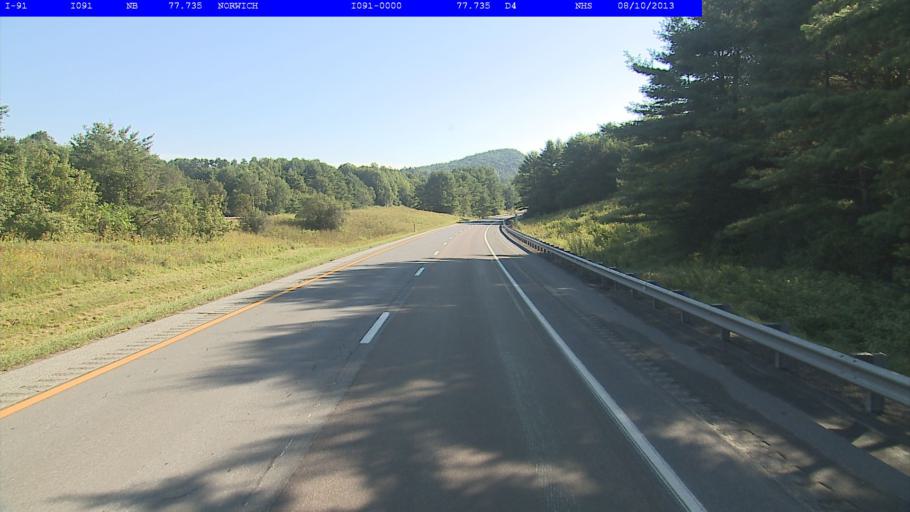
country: US
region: New Hampshire
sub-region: Grafton County
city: Hanover
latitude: 43.7384
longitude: -72.2708
